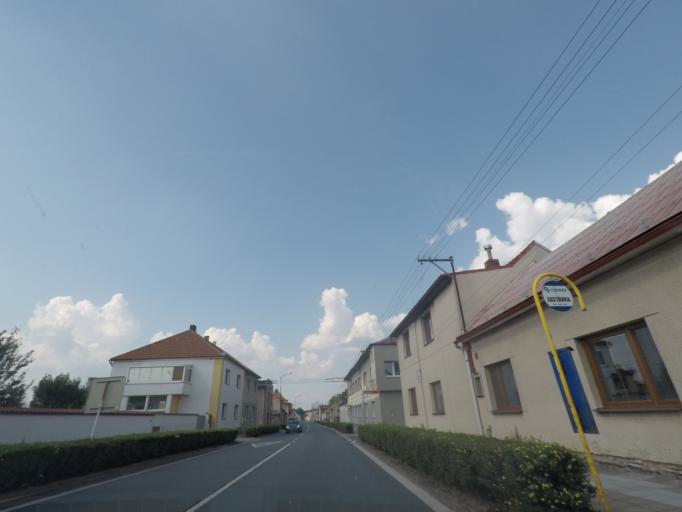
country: CZ
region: Pardubicky
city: Horni Jeleni
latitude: 50.0462
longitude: 16.0827
